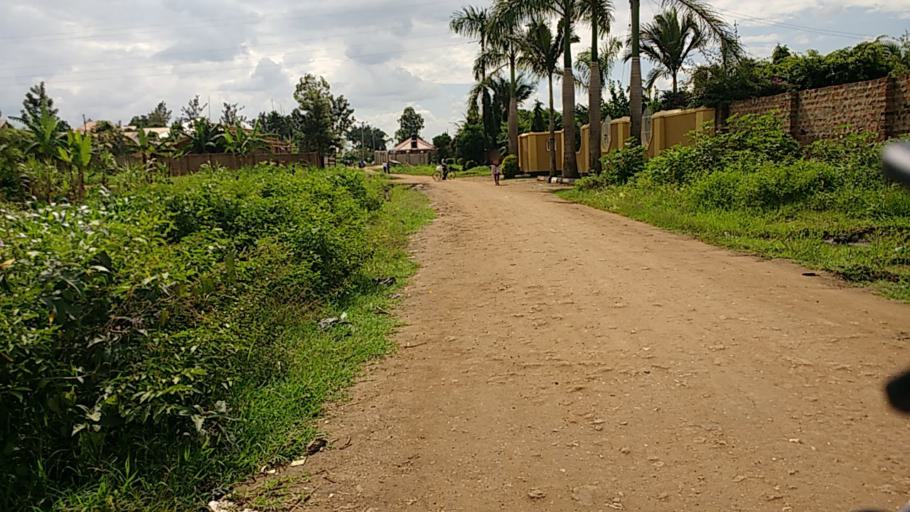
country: UG
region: Eastern Region
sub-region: Mbale District
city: Mbale
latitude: 1.0880
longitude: 34.1723
